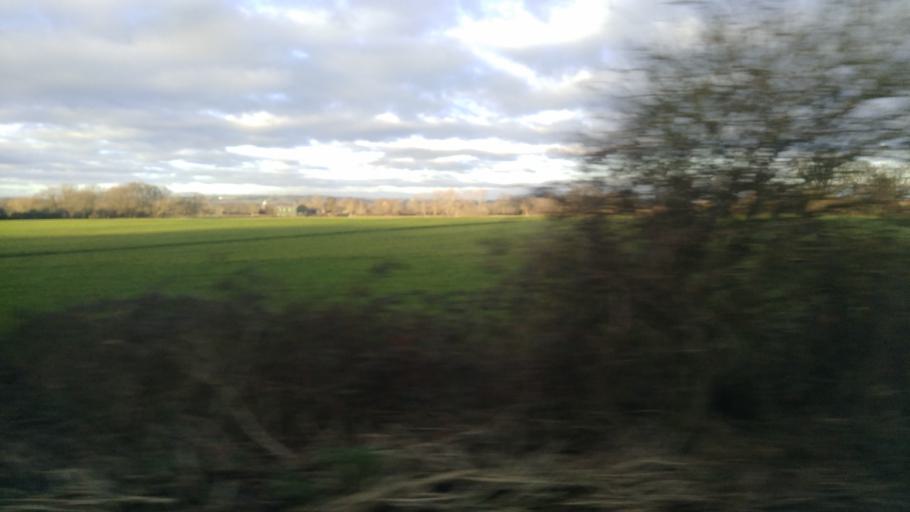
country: GB
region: England
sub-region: Kent
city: Headcorn
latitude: 51.1619
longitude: 0.6766
